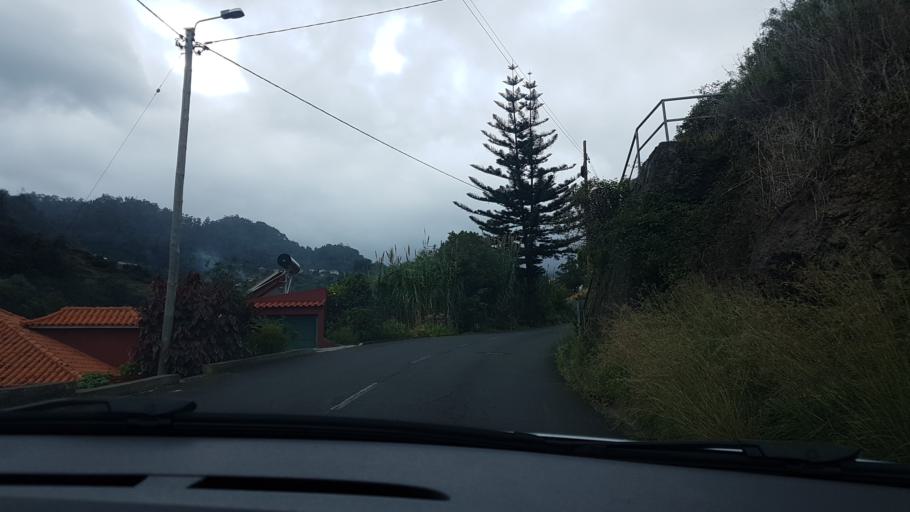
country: PT
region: Madeira
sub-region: Santana
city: Santana
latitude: 32.7726
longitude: -16.8329
